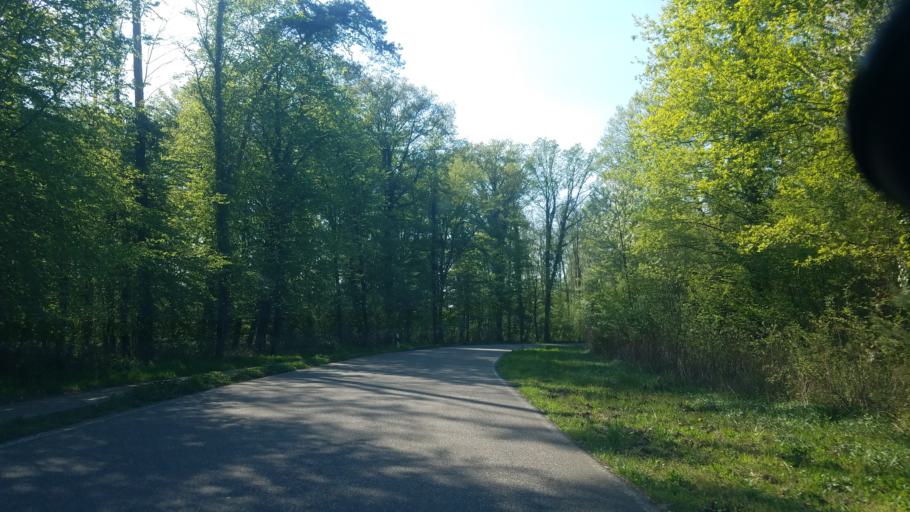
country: DE
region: Baden-Wuerttemberg
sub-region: Karlsruhe Region
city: Ottenhofen
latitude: 48.7658
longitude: 8.1144
